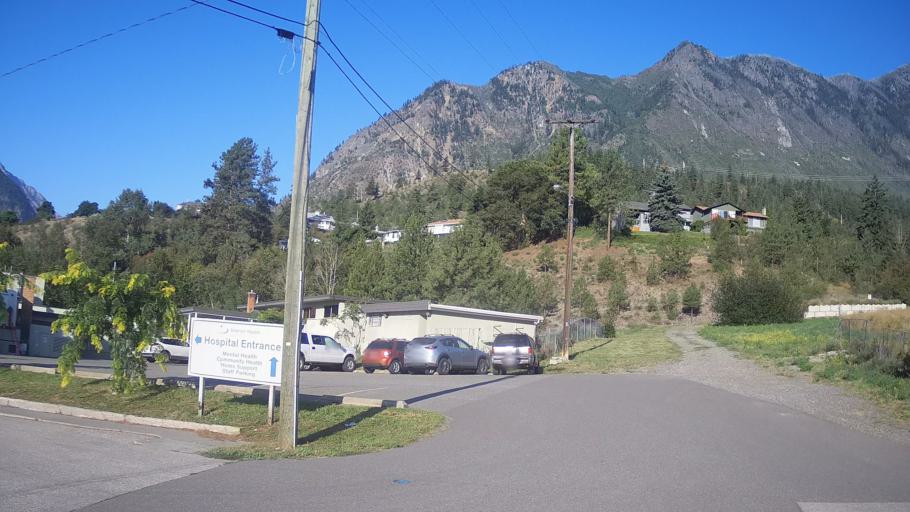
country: CA
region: British Columbia
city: Lillooet
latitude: 50.6899
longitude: -121.9401
